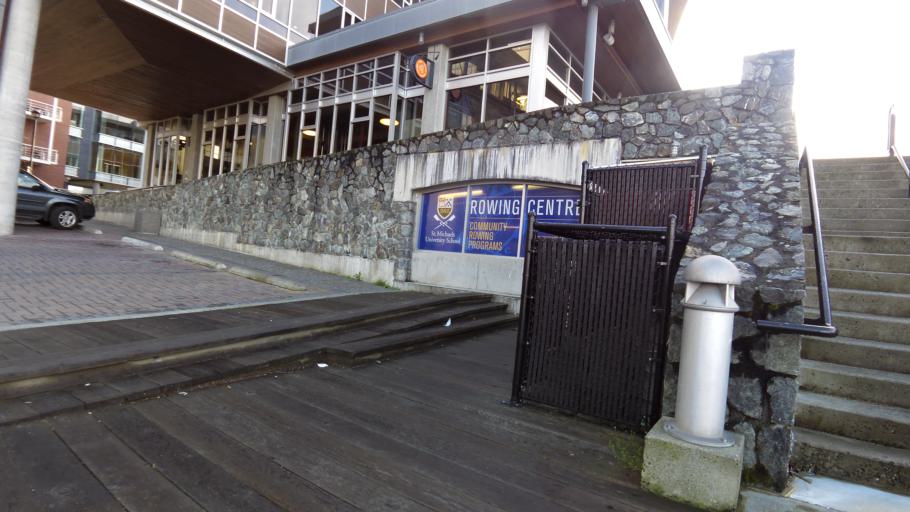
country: CA
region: British Columbia
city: Victoria
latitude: 48.4394
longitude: -123.3794
